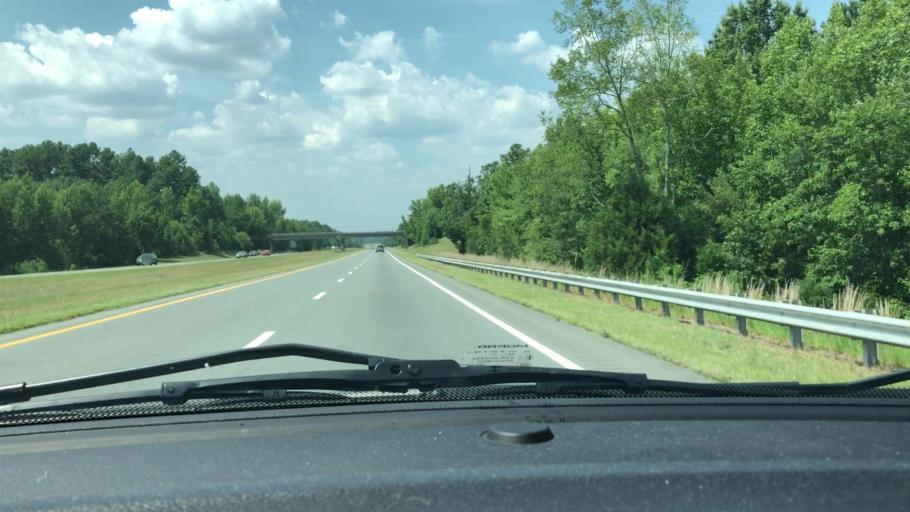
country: US
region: North Carolina
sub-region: Guilford County
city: Forest Oaks
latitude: 35.9312
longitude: -79.6821
